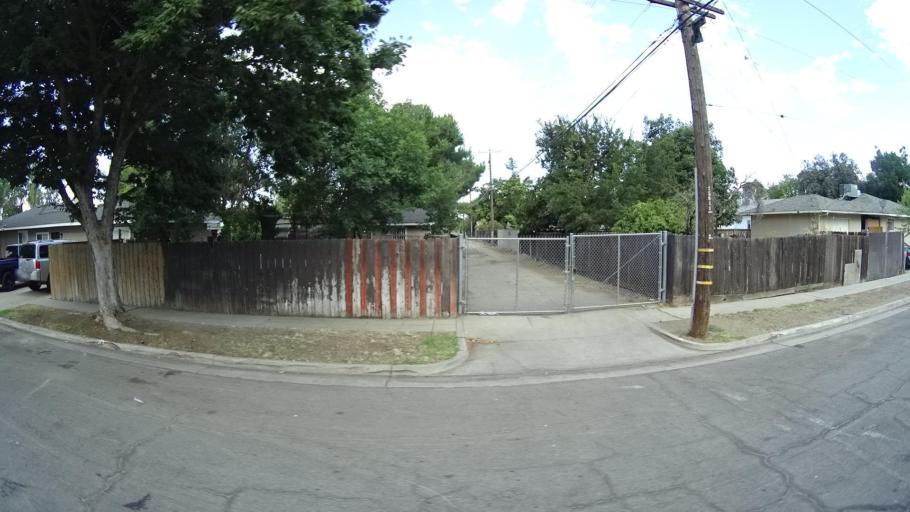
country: US
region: California
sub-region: Fresno County
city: Fresno
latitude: 36.7590
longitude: -119.7657
